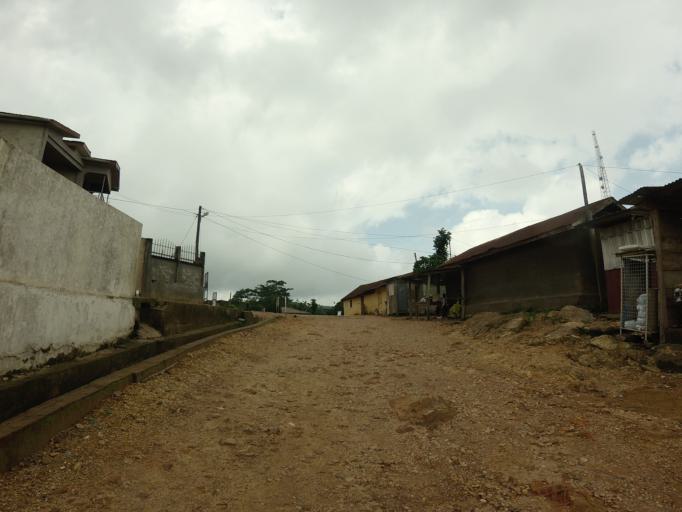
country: TG
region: Plateaux
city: Kpalime
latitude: 6.8442
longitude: 0.4354
